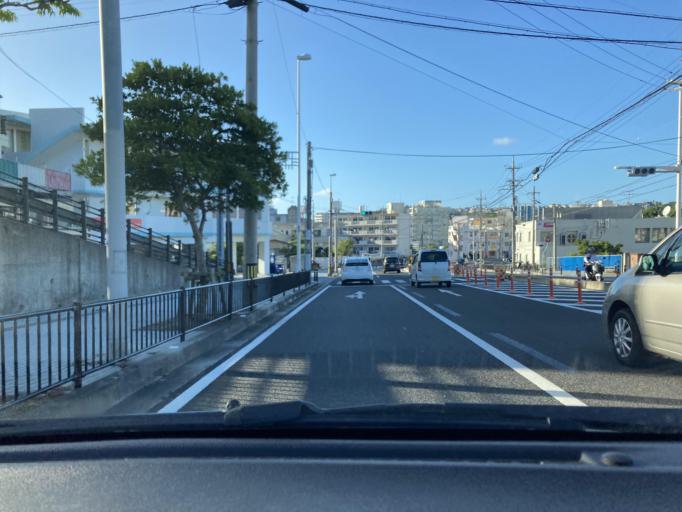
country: JP
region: Okinawa
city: Tomigusuku
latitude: 26.1917
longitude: 127.7287
